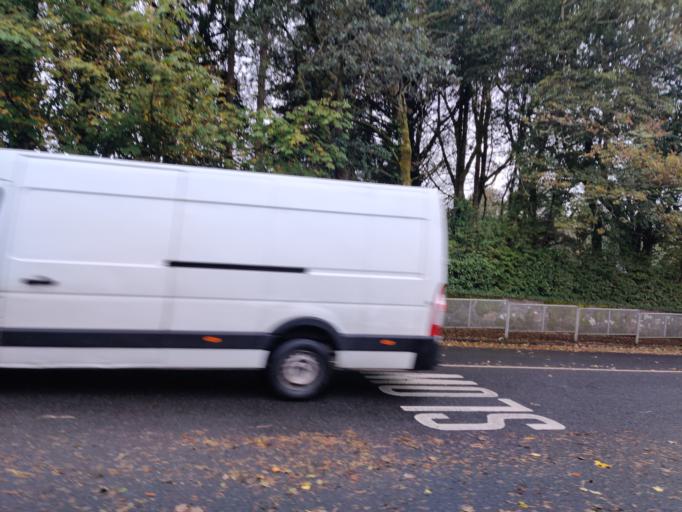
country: IE
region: Connaught
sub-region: Roscommon
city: Ballaghaderreen
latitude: 53.9009
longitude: -8.5852
